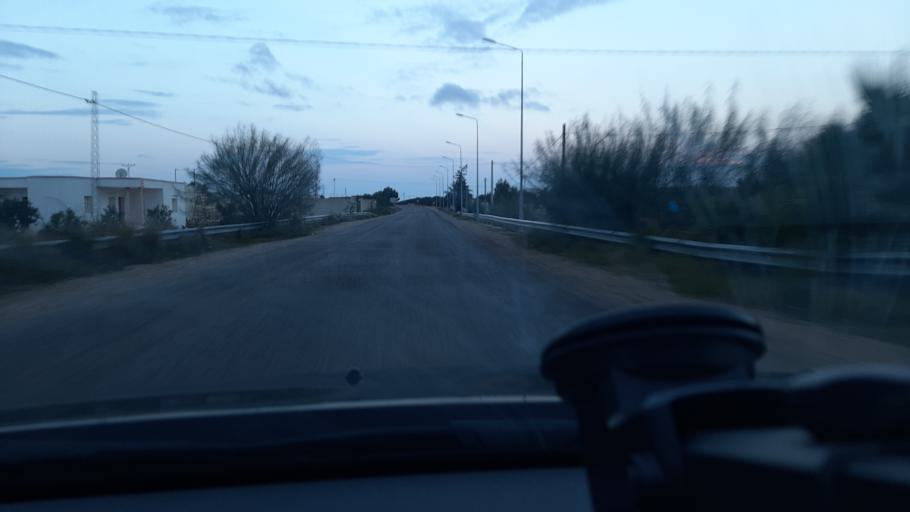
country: TN
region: Al Mahdiyah
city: Shurban
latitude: 34.9718
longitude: 10.3736
